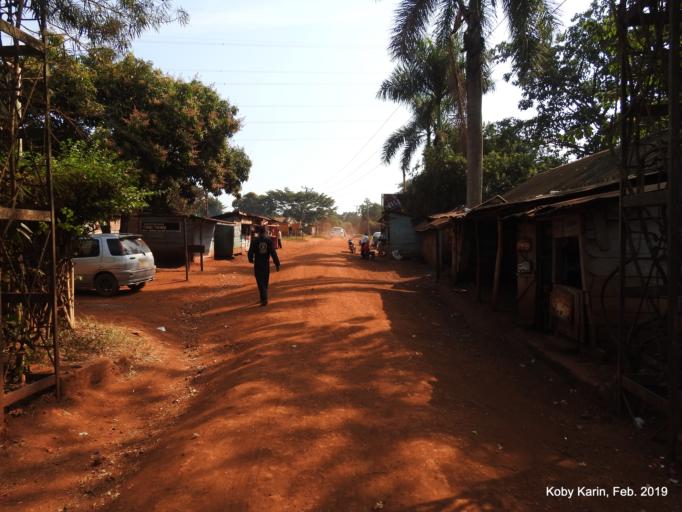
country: UG
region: Eastern Region
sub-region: Jinja District
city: Jinja
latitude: 0.4847
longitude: 33.1630
